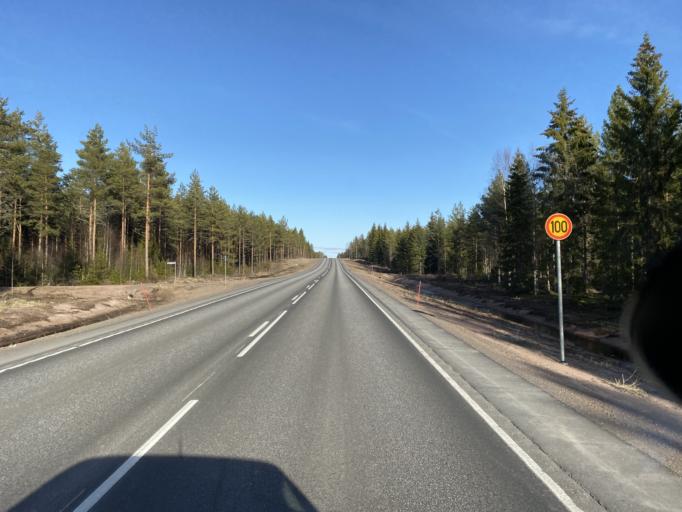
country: FI
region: Satakunta
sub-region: Rauma
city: Koeylioe
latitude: 61.1654
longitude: 22.3741
